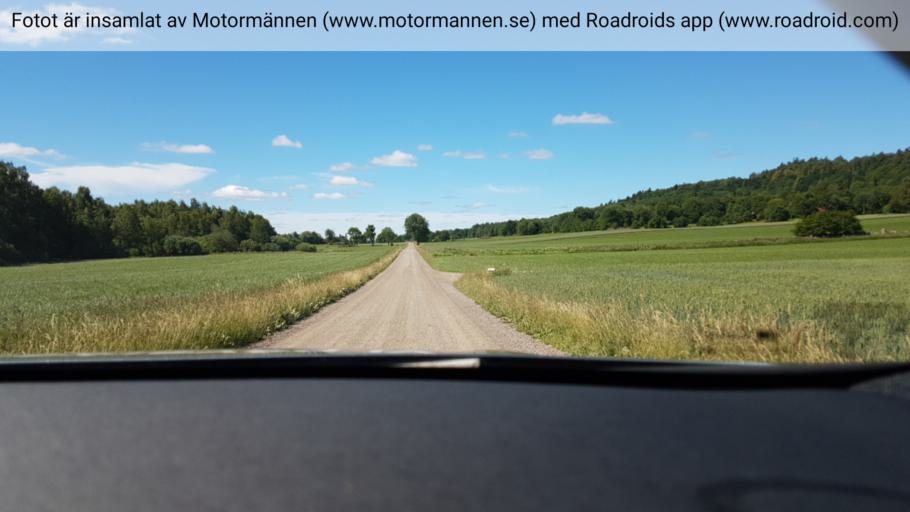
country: SE
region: Vaestra Goetaland
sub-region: Falkopings Kommun
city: Akarp
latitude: 58.2228
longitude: 13.7739
